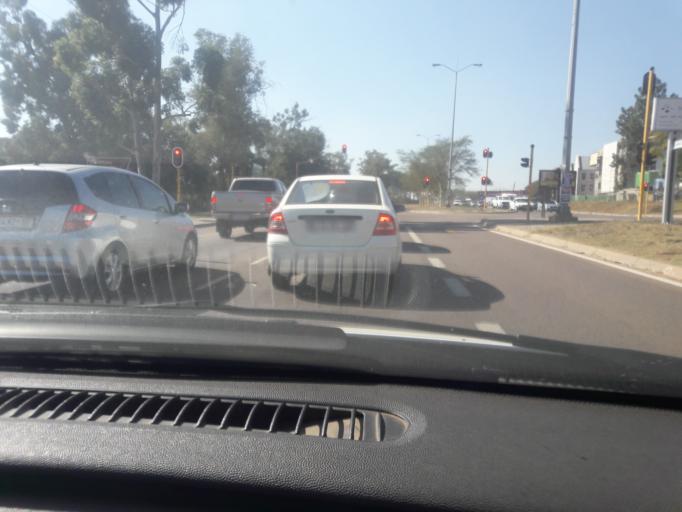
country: ZA
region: Gauteng
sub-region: City of Tshwane Metropolitan Municipality
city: Pretoria
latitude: -25.7657
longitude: 28.3107
